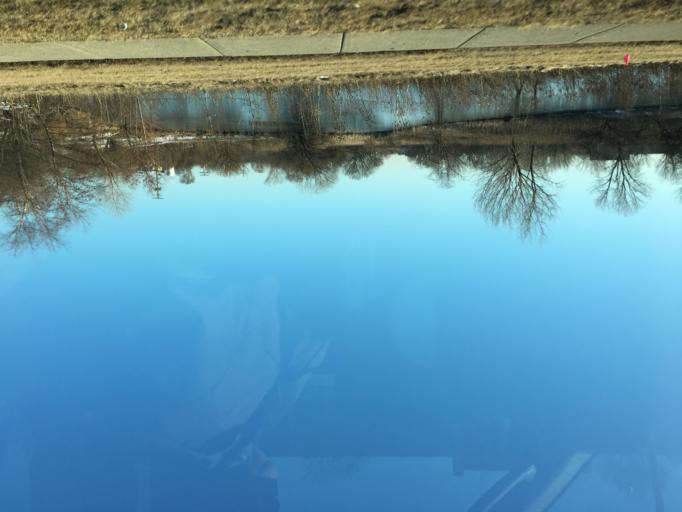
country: US
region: Illinois
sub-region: Cook County
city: Hoffman Estates
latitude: 42.0724
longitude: -88.0564
